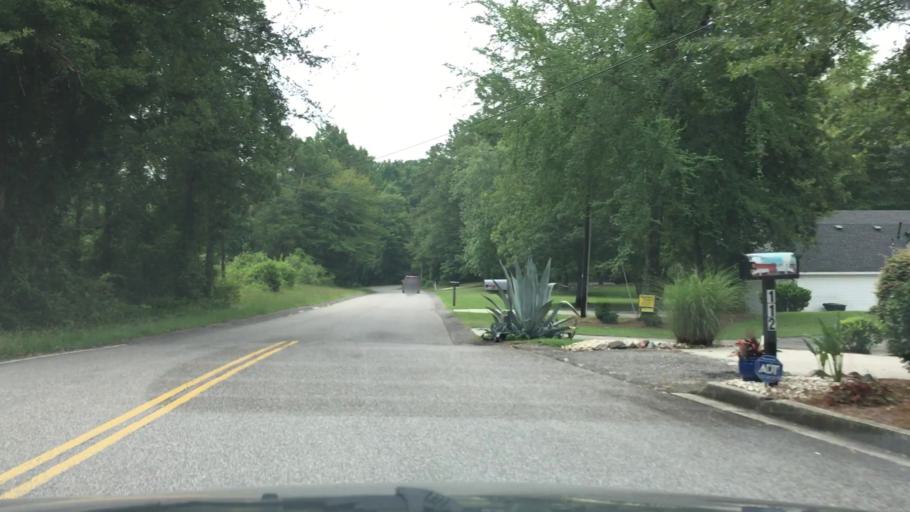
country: US
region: South Carolina
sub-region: Aiken County
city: Belvedere
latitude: 33.5436
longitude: -81.9593
